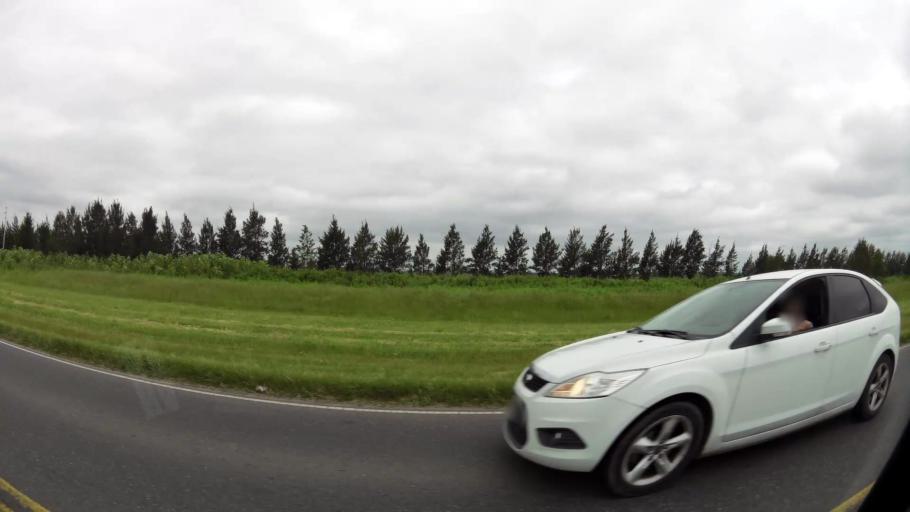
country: AR
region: Buenos Aires
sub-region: Partido de San Vicente
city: San Vicente
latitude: -35.0133
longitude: -58.4690
